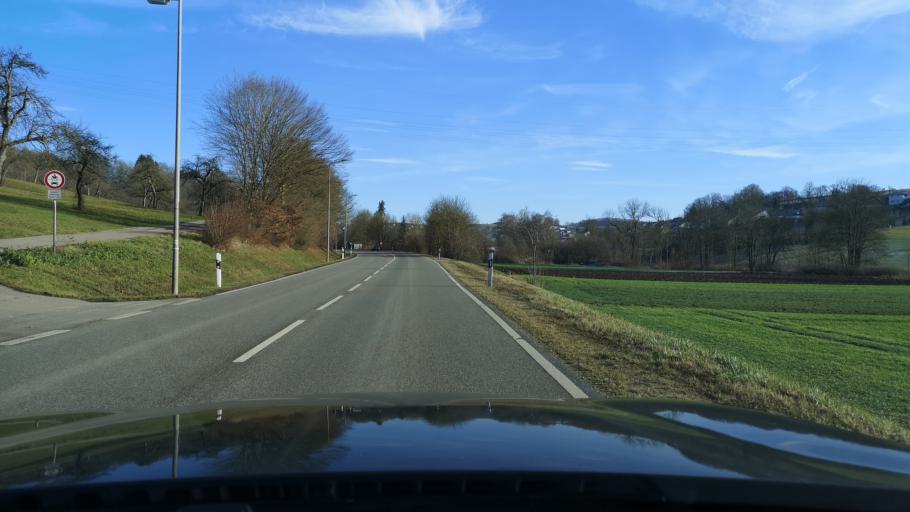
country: DE
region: Baden-Wuerttemberg
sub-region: Regierungsbezirk Stuttgart
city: Huttlingen
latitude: 48.8937
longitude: 10.0848
